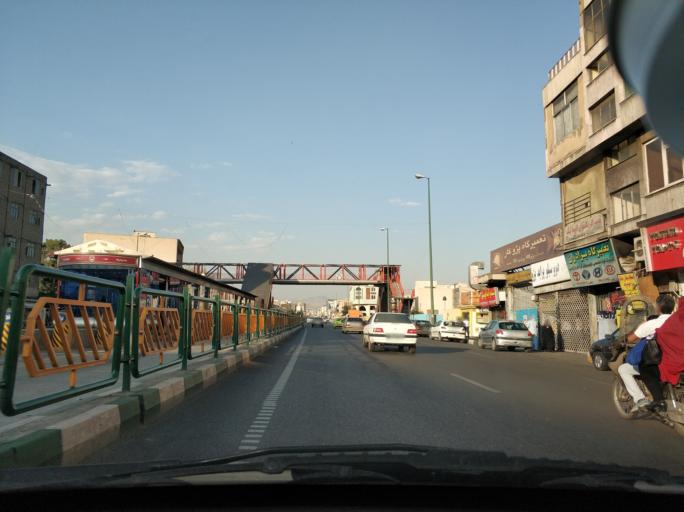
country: IR
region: Tehran
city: Tehran
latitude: 35.7110
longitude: 51.4788
